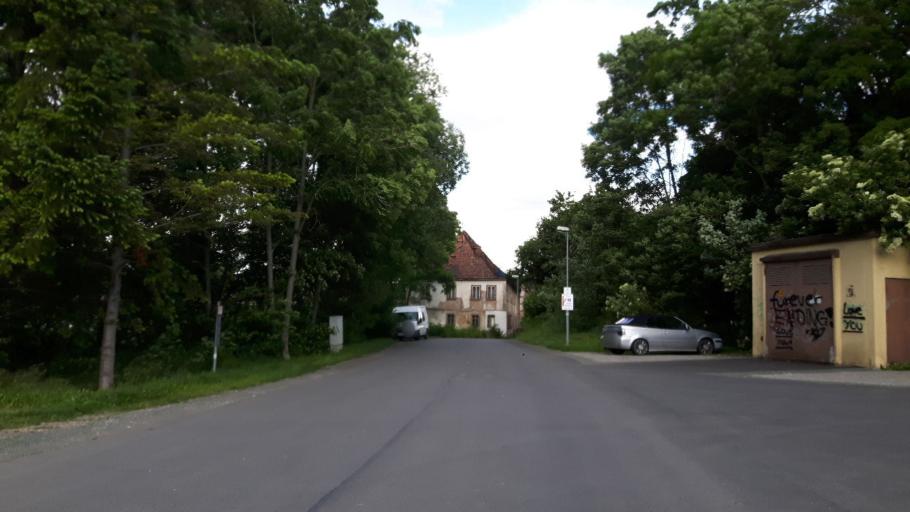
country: DE
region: Thuringia
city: Kranichfeld
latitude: 50.8548
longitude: 11.2041
